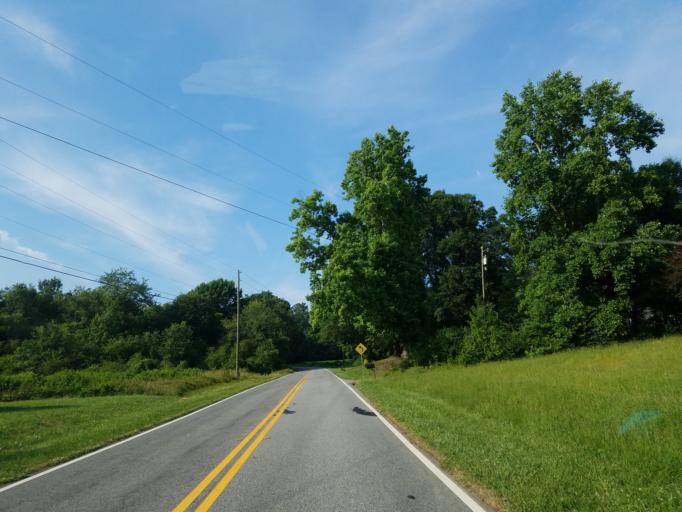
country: US
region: Georgia
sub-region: Forsyth County
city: Cumming
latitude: 34.2886
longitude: -84.0677
